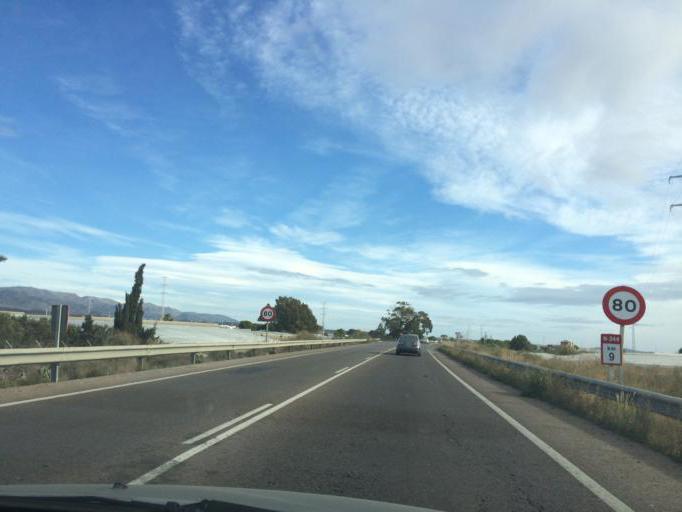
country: ES
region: Andalusia
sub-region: Provincia de Almeria
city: Retamar
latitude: 36.8548
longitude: -2.3680
